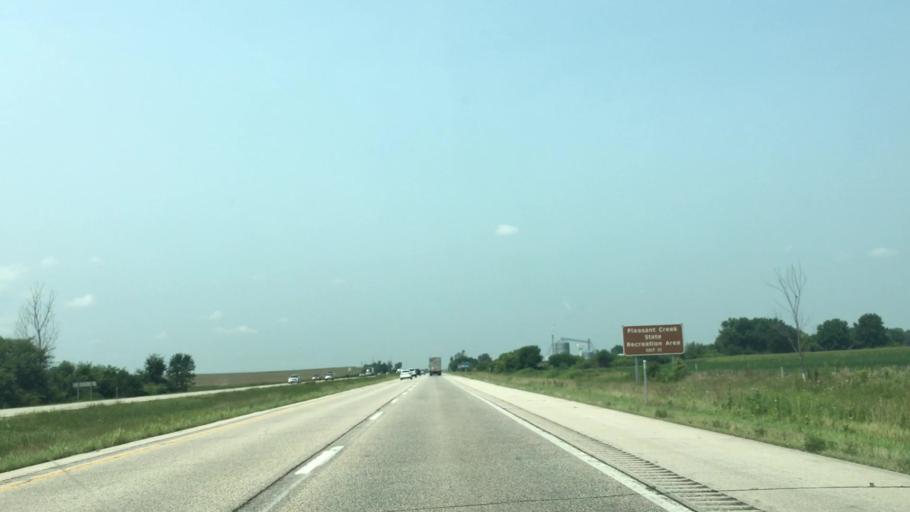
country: US
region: Iowa
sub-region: Linn County
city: Center Point
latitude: 42.1616
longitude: -91.7632
